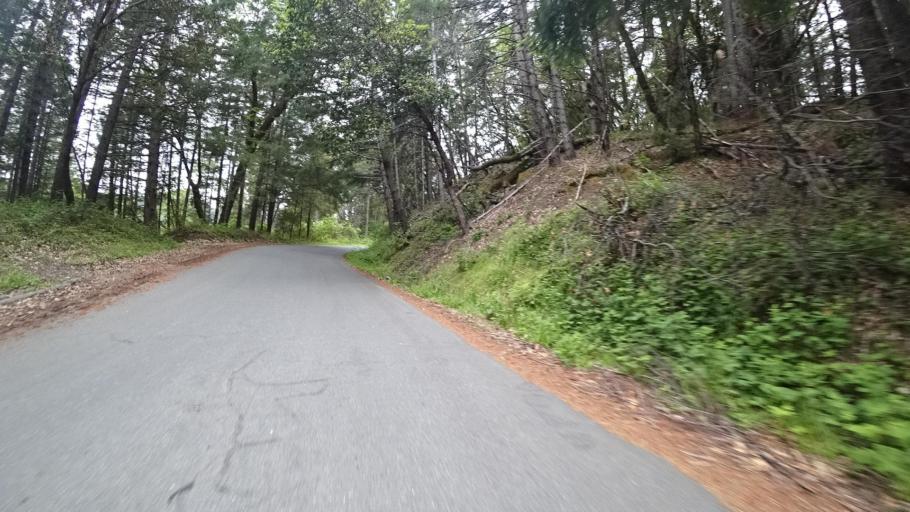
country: US
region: California
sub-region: Humboldt County
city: Willow Creek
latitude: 41.1039
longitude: -123.7092
